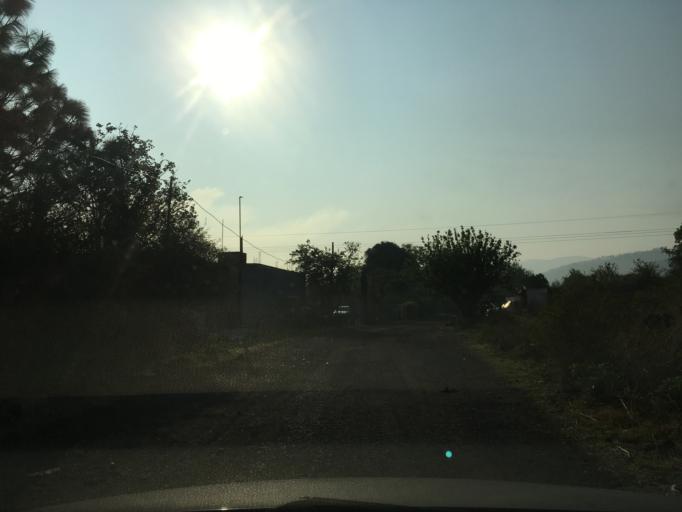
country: MX
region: Michoacan
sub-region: Morelia
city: La Mintzita (Piedra Dura)
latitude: 19.6454
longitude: -101.2780
